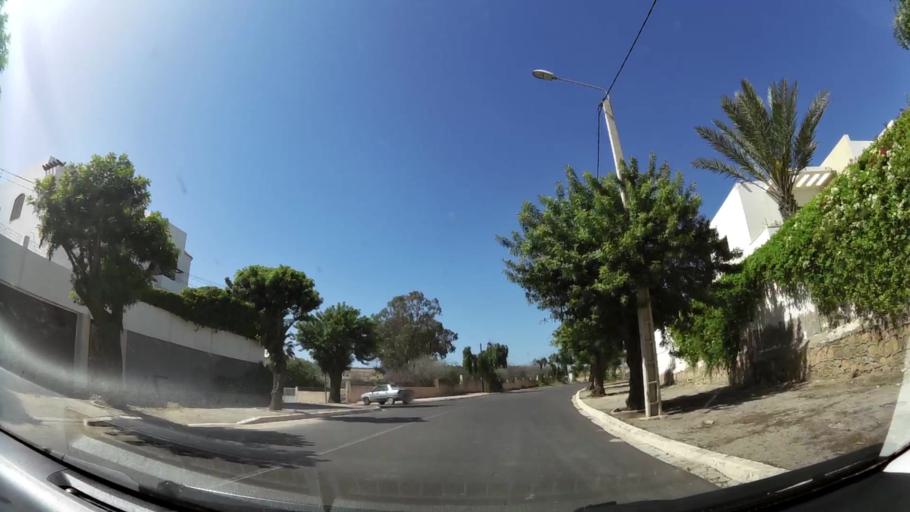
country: MA
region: Souss-Massa-Draa
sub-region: Agadir-Ida-ou-Tnan
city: Agadir
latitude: 30.4275
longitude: -9.6016
